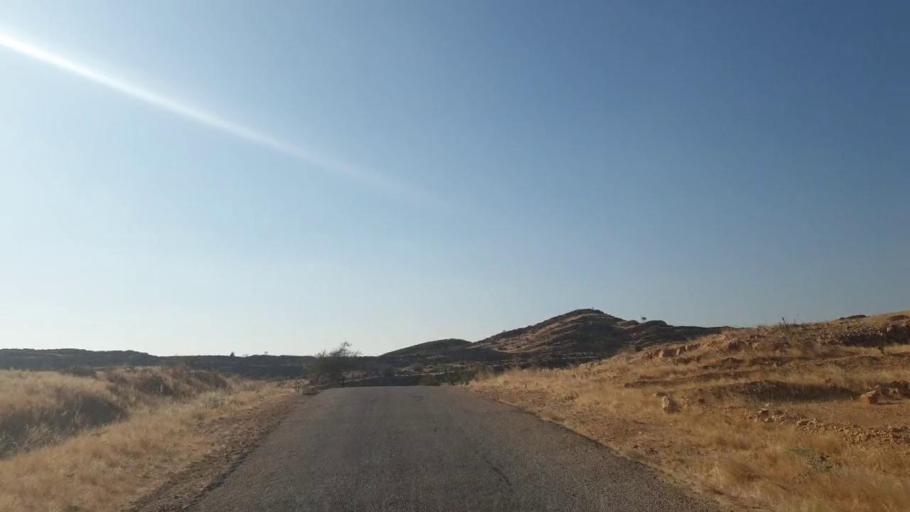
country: PK
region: Sindh
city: Malir Cantonment
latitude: 25.4026
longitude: 67.4865
